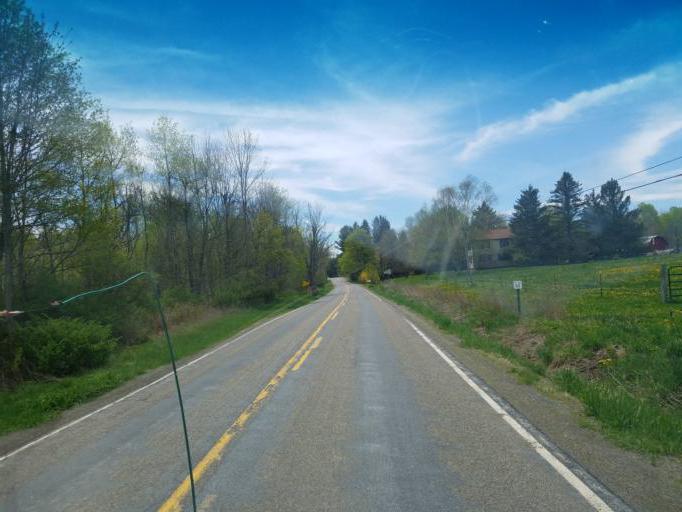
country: US
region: Pennsylvania
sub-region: Tioga County
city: Wellsboro
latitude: 41.7032
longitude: -77.4104
